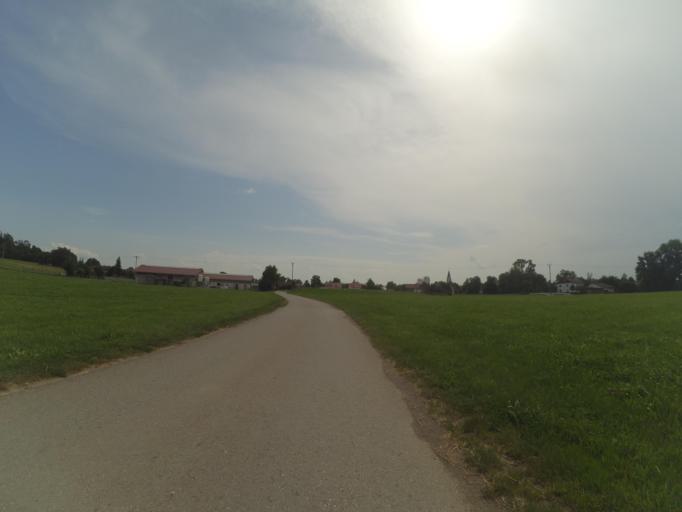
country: DE
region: Bavaria
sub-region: Swabia
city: Jengen
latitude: 48.0041
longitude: 10.7271
